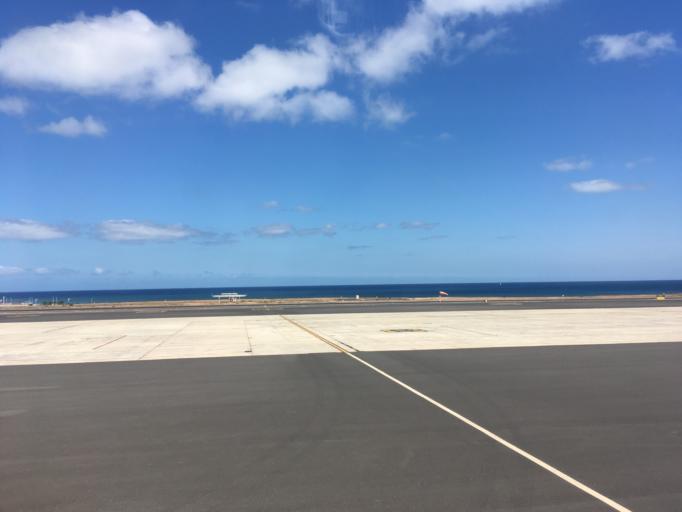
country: ES
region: Canary Islands
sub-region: Provincia de Las Palmas
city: Tias
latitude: 28.9504
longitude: -13.6063
